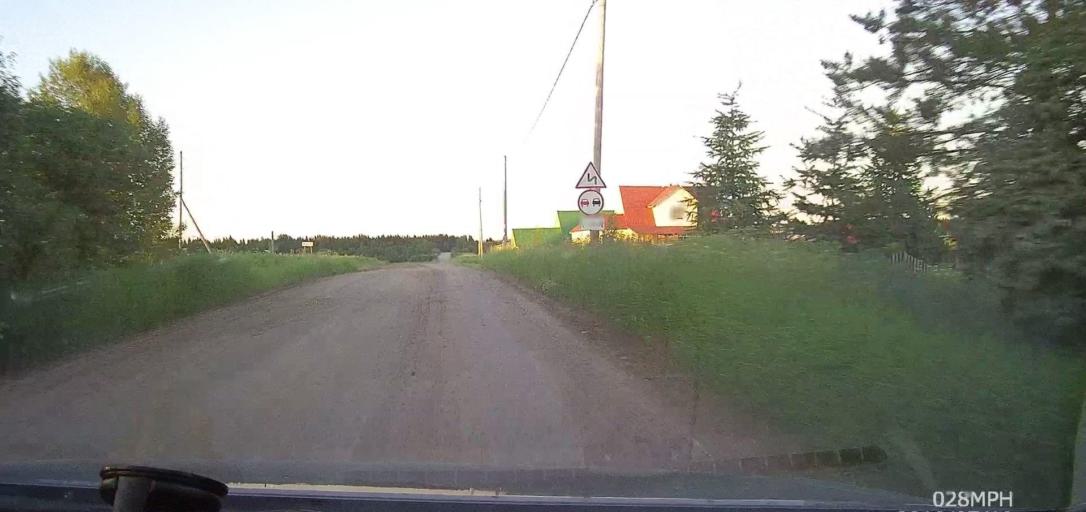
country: RU
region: Arkhangelskaya
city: Lukovetskiy
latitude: 64.2345
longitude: 42.7063
